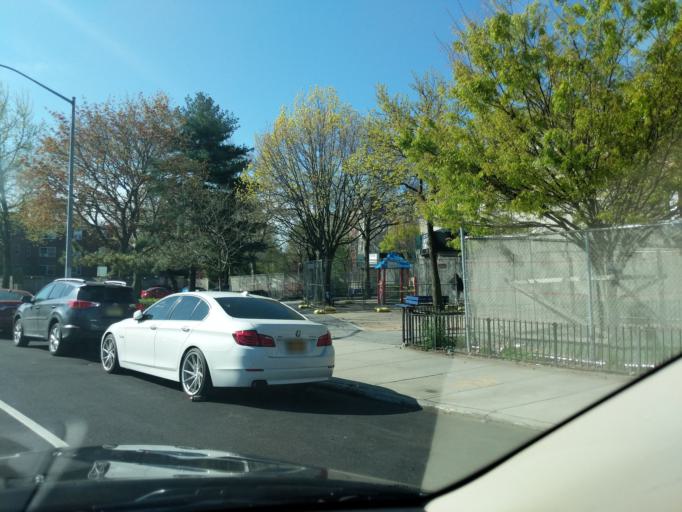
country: US
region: New York
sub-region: Kings County
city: East New York
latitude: 40.6518
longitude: -73.8932
